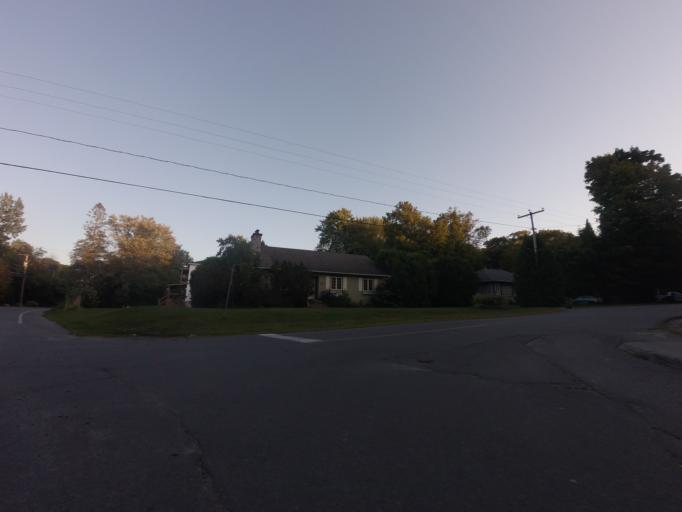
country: CA
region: Quebec
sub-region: Monteregie
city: Hudson
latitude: 45.4547
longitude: -74.1357
